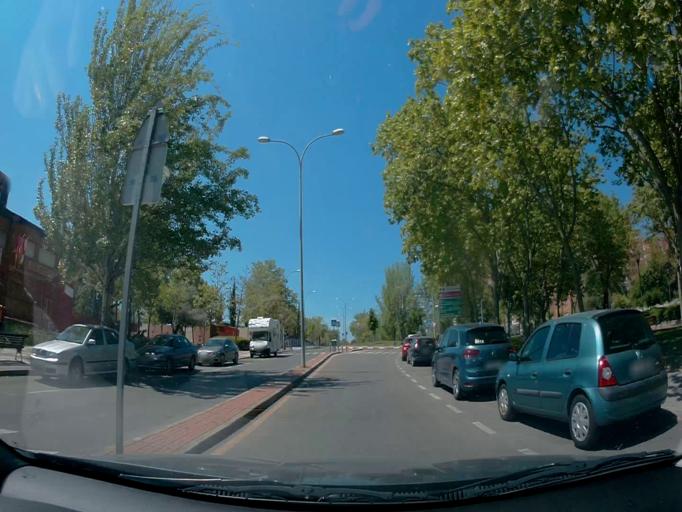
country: ES
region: Madrid
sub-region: Provincia de Madrid
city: Alcorcon
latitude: 40.3402
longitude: -3.8205
